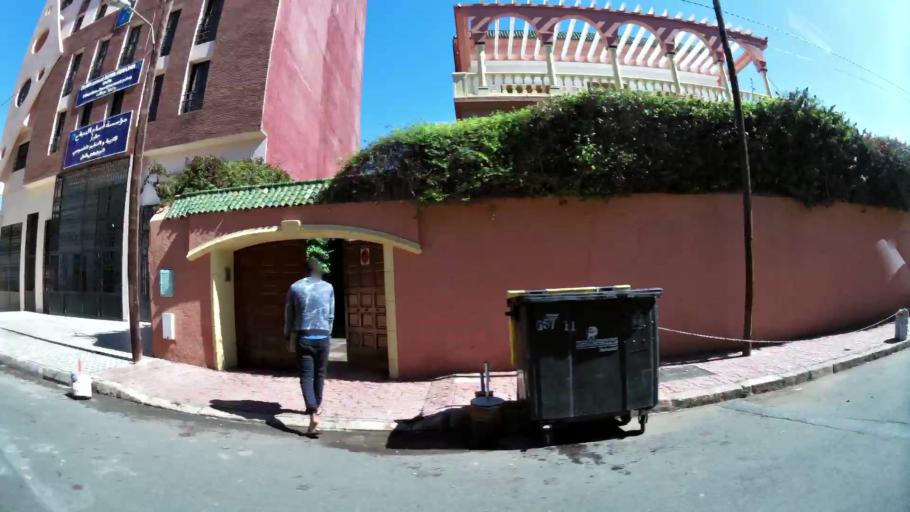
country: MA
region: Marrakech-Tensift-Al Haouz
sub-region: Marrakech
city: Marrakesh
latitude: 31.6373
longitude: -8.0063
